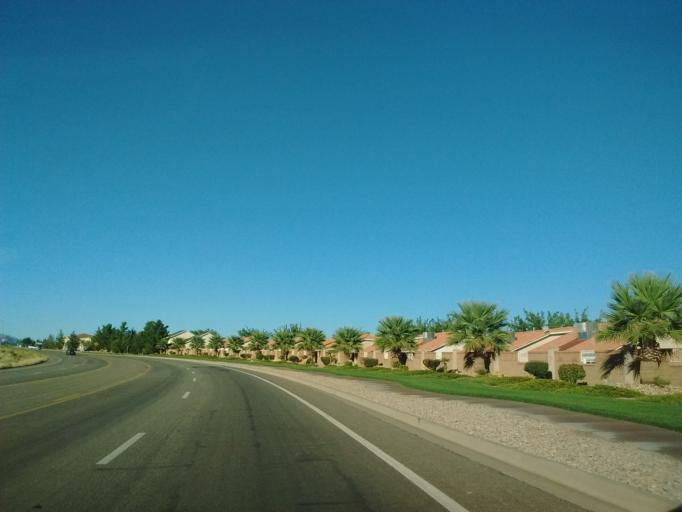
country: US
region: Utah
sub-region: Washington County
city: Washington
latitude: 37.1575
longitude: -113.4366
